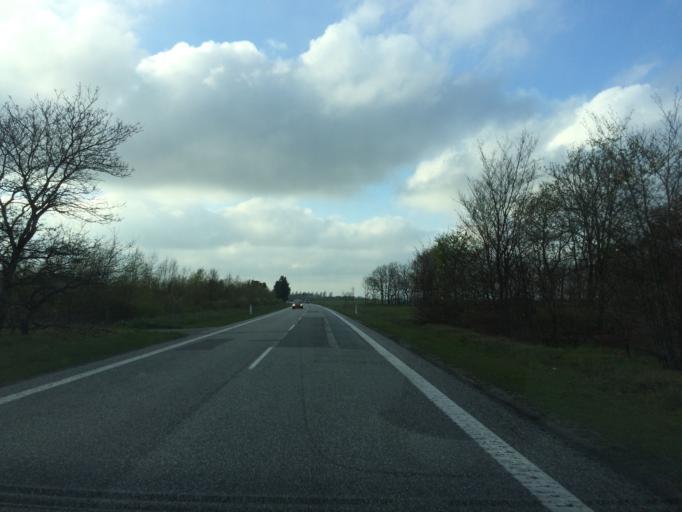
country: DK
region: Central Jutland
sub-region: Viborg Kommune
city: Karup
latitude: 56.3244
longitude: 9.1108
